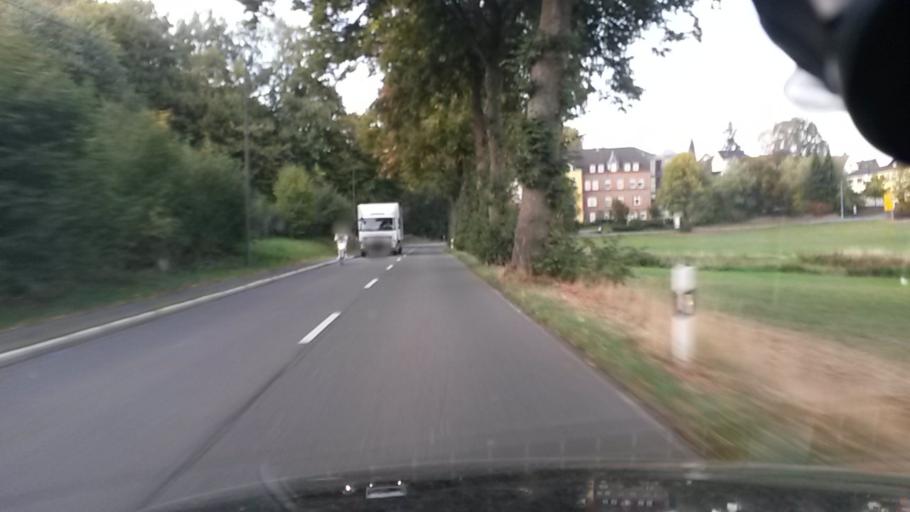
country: DE
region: North Rhine-Westphalia
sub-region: Regierungsbezirk Koln
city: Marienheide
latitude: 51.0801
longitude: 7.5244
